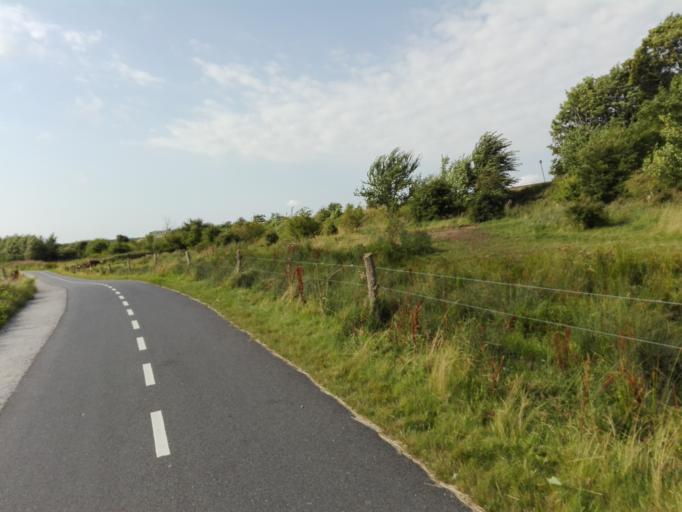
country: DK
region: Central Jutland
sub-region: Arhus Kommune
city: Lystrup
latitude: 56.2200
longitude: 10.2075
